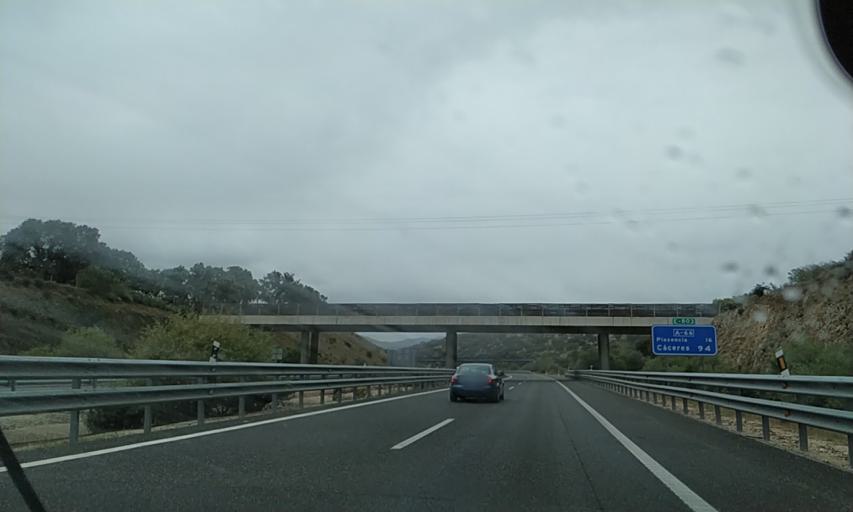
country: ES
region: Extremadura
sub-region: Provincia de Caceres
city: Villar de Plasencia
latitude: 40.1363
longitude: -6.0447
